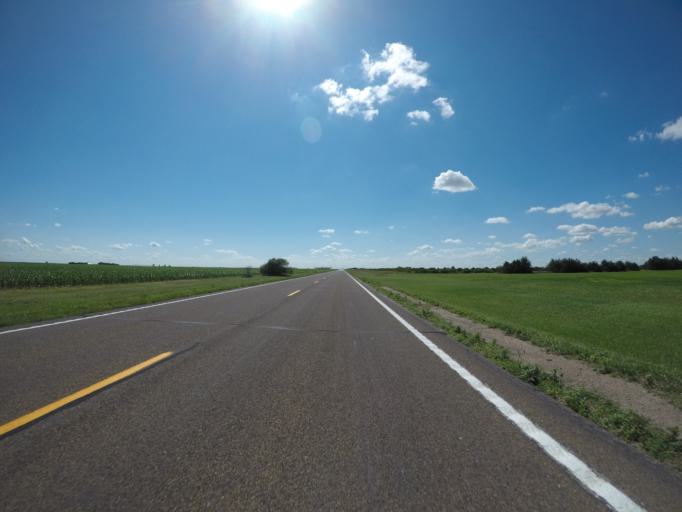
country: US
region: Nebraska
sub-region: Chase County
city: Imperial
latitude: 40.5377
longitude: -101.8833
